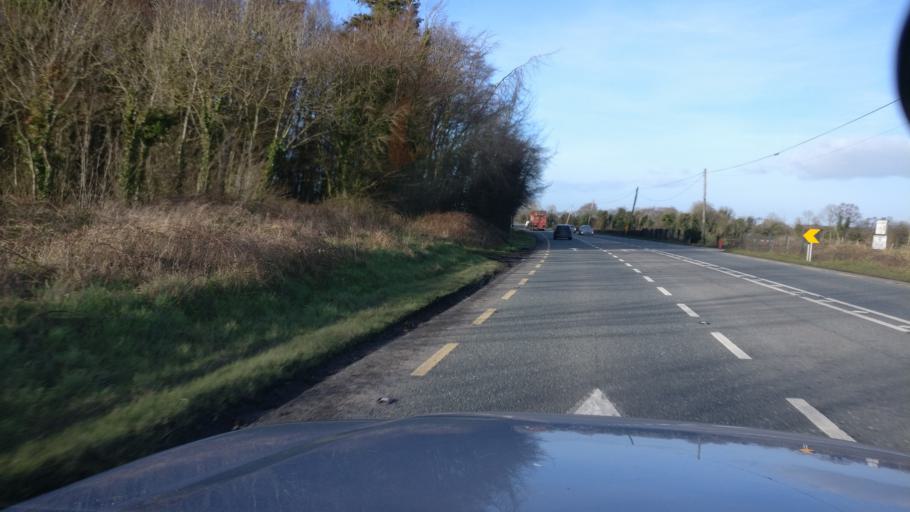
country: IE
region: Leinster
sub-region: Uibh Fhaili
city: Tullamore
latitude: 53.2314
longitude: -7.4757
